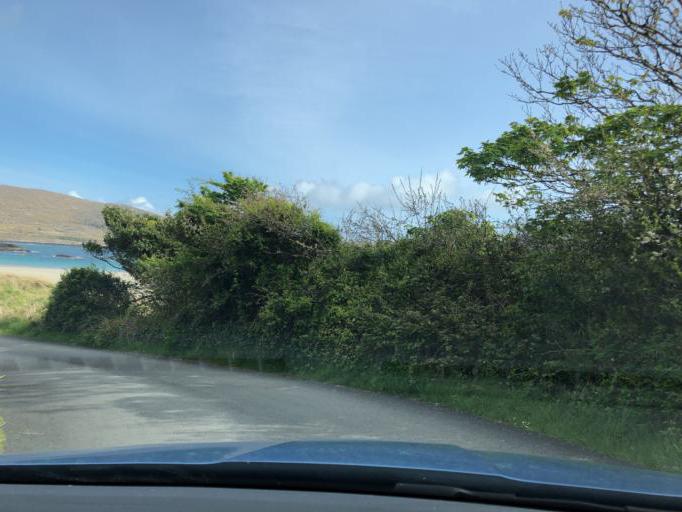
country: IE
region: Munster
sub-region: Ciarrai
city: Cahersiveen
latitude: 51.7607
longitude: -10.1385
